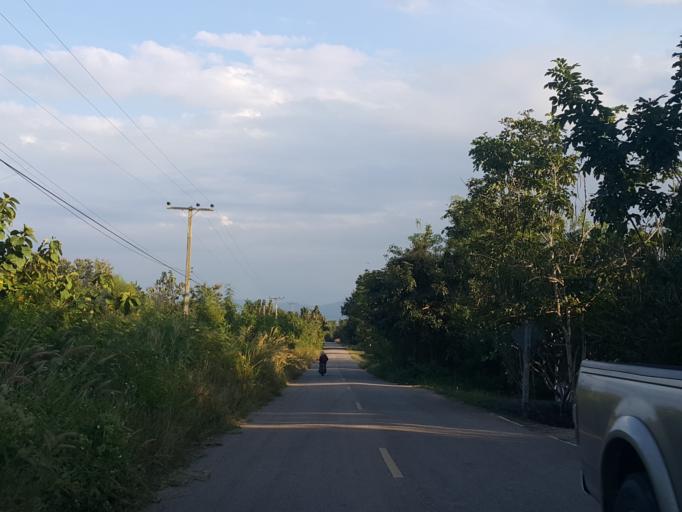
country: TH
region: Lampang
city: Lampang
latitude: 18.4212
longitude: 99.5463
